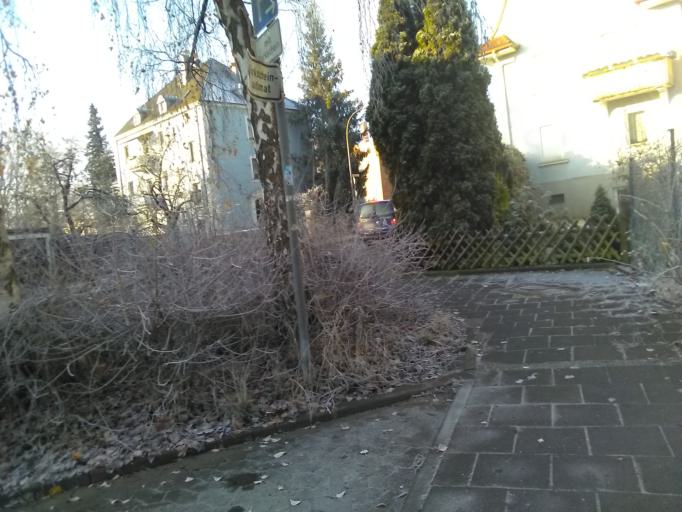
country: DE
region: Bavaria
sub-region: Upper Franconia
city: Forchheim
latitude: 49.7163
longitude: 11.0661
